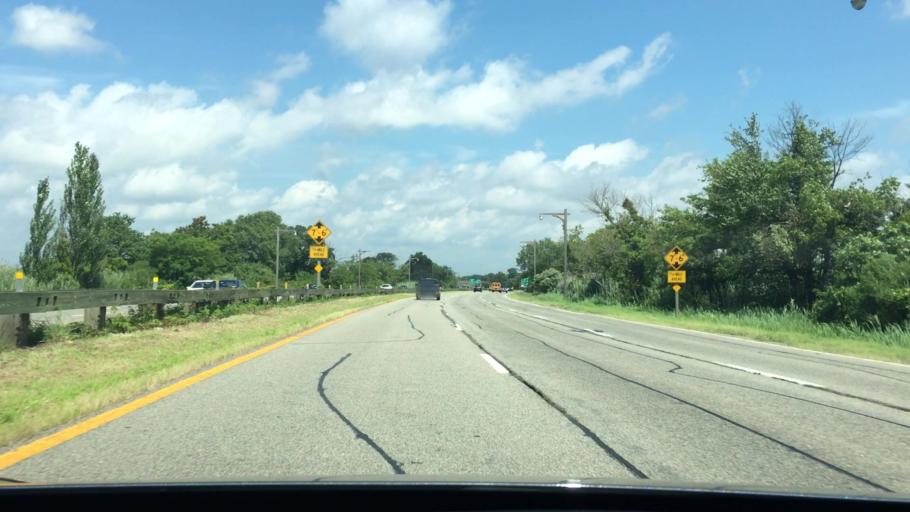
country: US
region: New York
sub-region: Nassau County
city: Freeport
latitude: 40.6458
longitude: -73.5655
